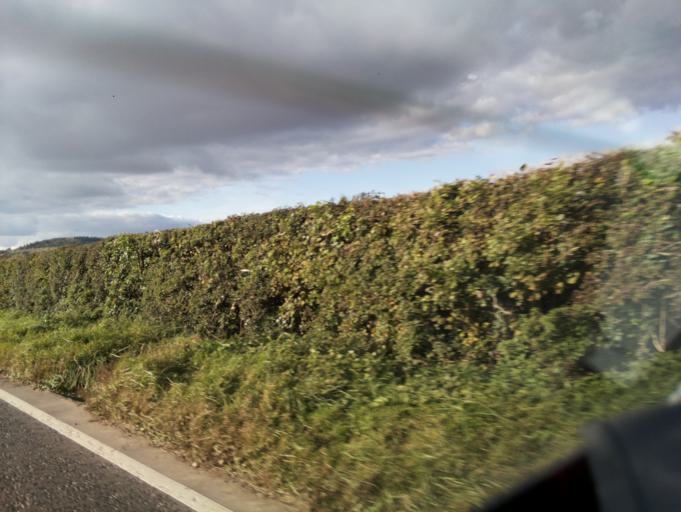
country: GB
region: England
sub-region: Herefordshire
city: Bridge Sollers
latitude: 52.0755
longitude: -2.8408
